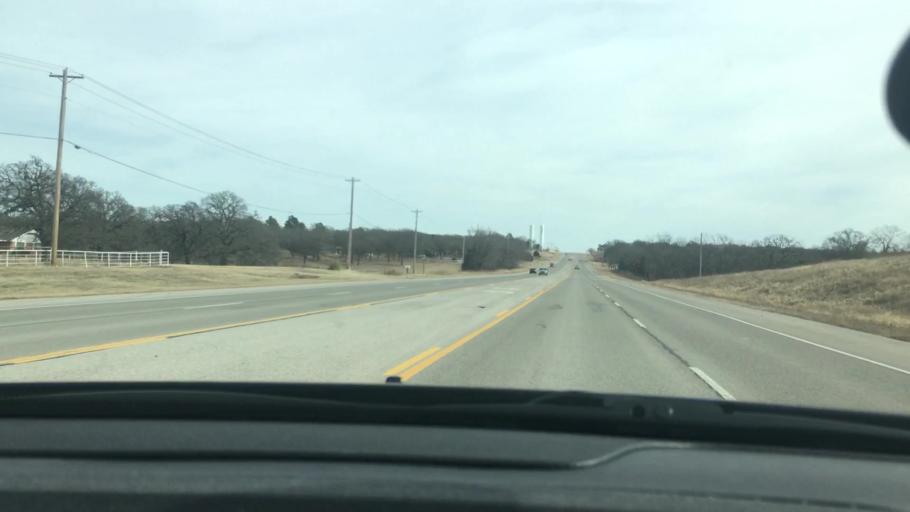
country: US
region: Oklahoma
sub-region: Carter County
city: Dickson
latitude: 34.1871
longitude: -97.0116
